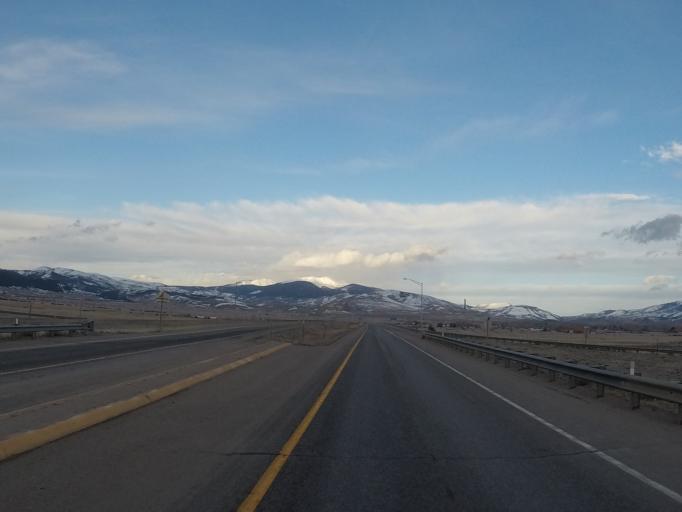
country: US
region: Montana
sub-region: Deer Lodge County
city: Warm Springs
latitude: 46.0955
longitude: -112.7943
